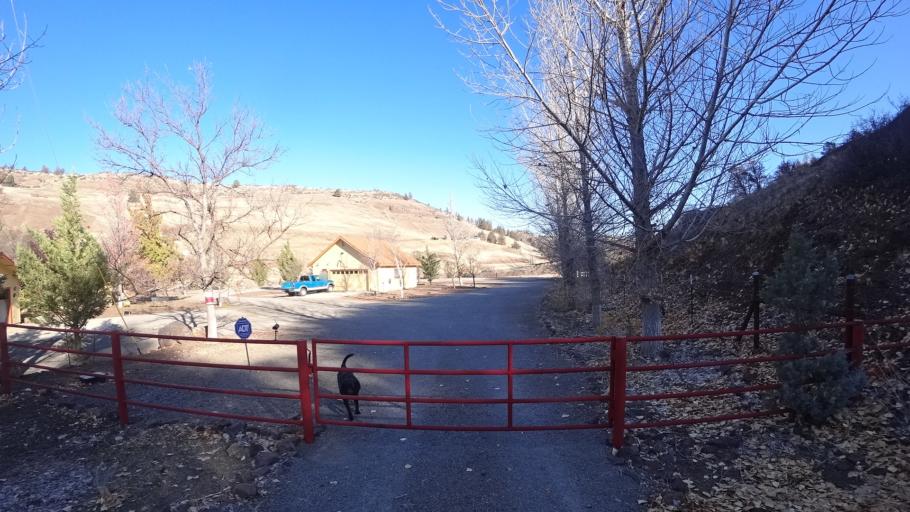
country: US
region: California
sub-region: Siskiyou County
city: Montague
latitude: 41.9245
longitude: -122.4471
